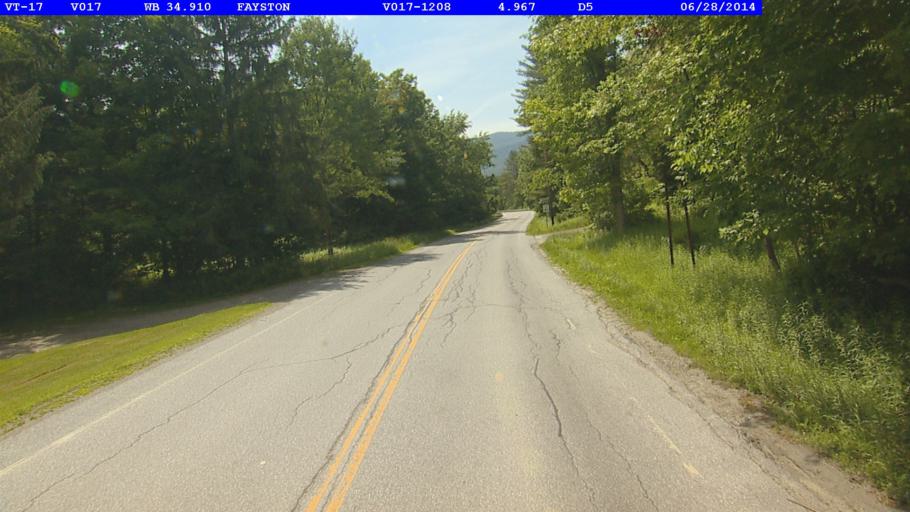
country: US
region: Vermont
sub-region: Washington County
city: Waterbury
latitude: 44.1824
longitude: -72.8597
